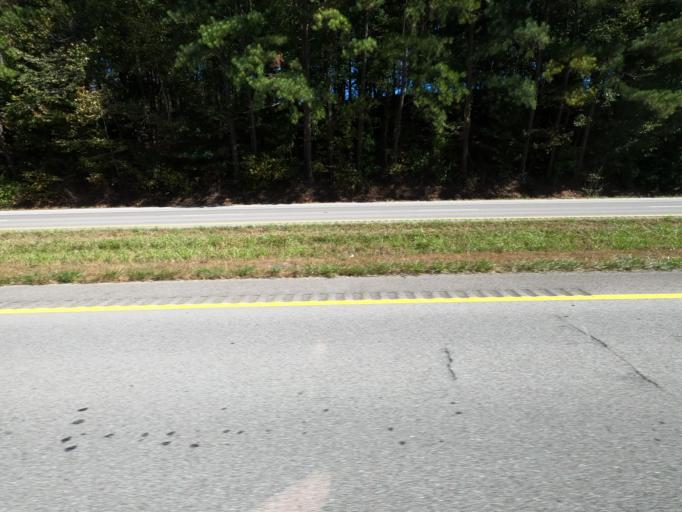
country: US
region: Tennessee
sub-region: Maury County
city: Mount Pleasant
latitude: 35.4034
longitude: -87.2802
